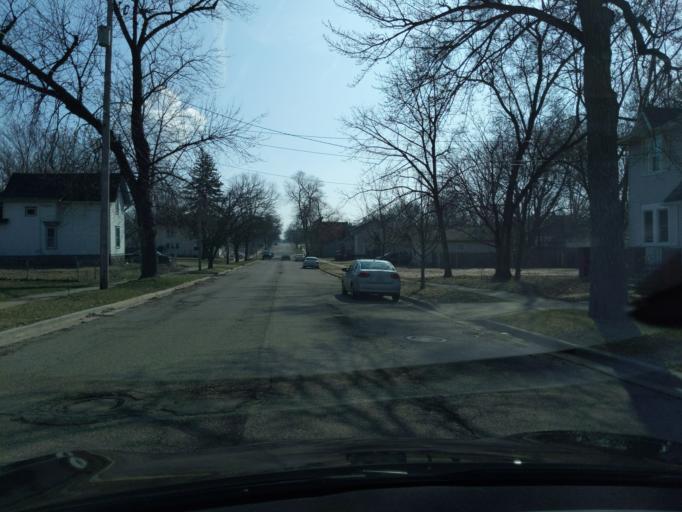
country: US
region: Michigan
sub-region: Jackson County
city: Jackson
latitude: 42.2422
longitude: -84.4139
